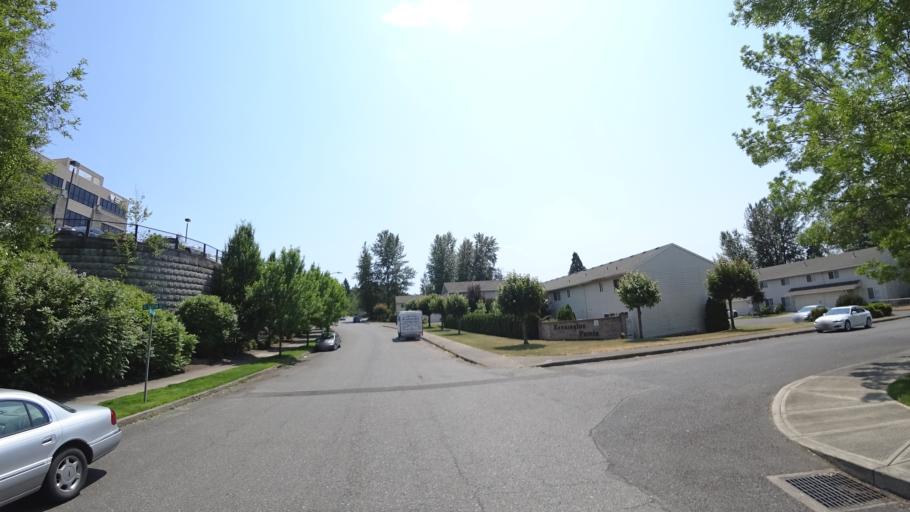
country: US
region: Oregon
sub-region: Multnomah County
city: Lents
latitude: 45.4557
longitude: -122.5699
